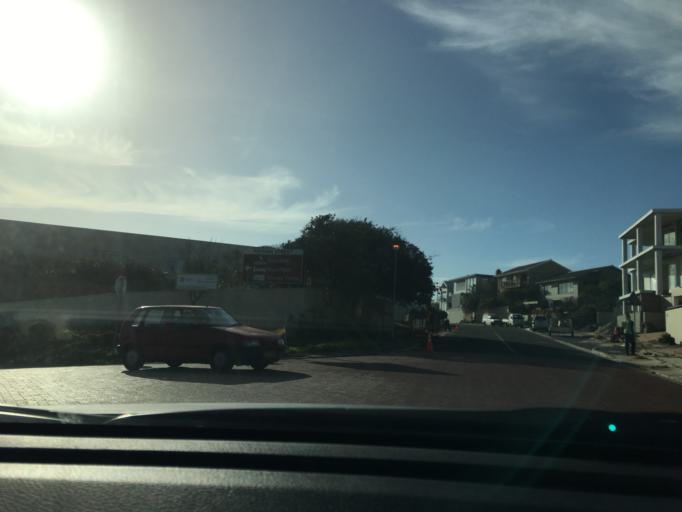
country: ZA
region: Western Cape
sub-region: City of Cape Town
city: Sunset Beach
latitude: -33.7975
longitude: 18.4599
